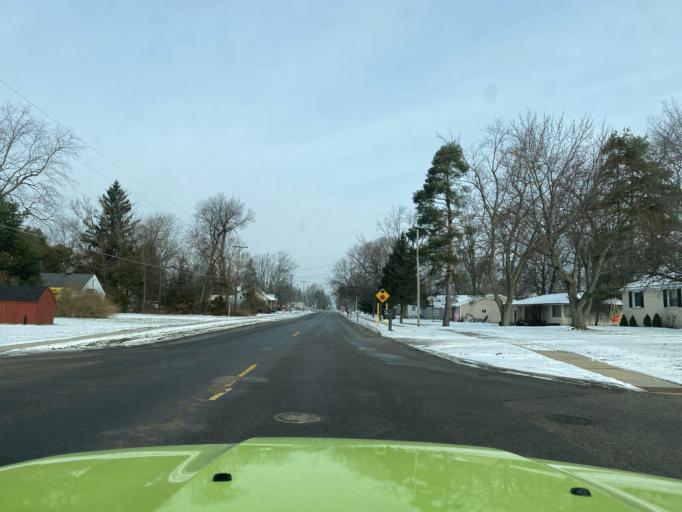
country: US
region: Michigan
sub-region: Ottawa County
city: Allendale
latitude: 42.9698
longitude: -85.9243
